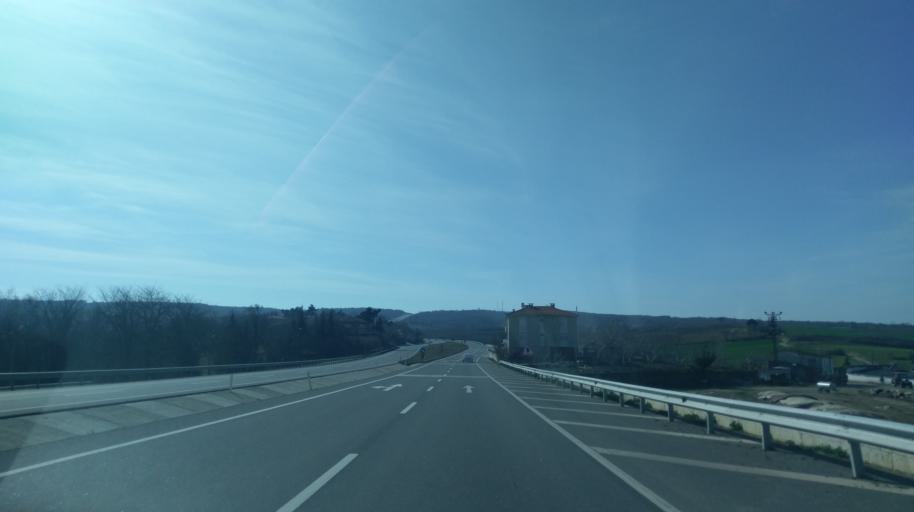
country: TR
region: Edirne
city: Ibriktepe
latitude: 40.9934
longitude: 26.6376
